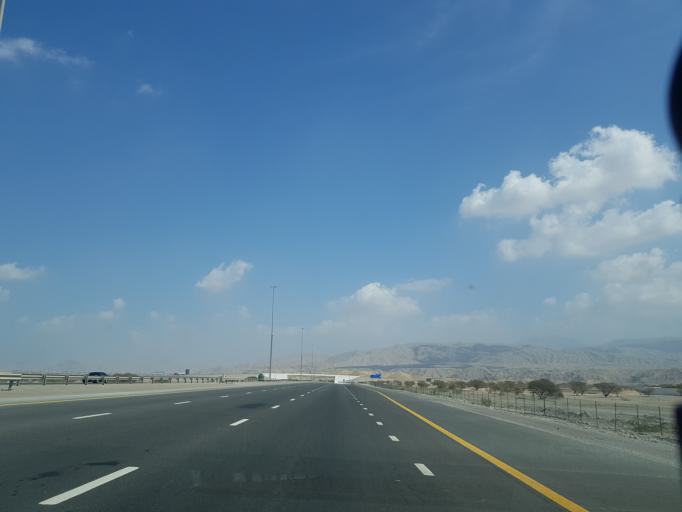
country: AE
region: Ra's al Khaymah
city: Ras al-Khaimah
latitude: 25.7120
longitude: 56.0025
